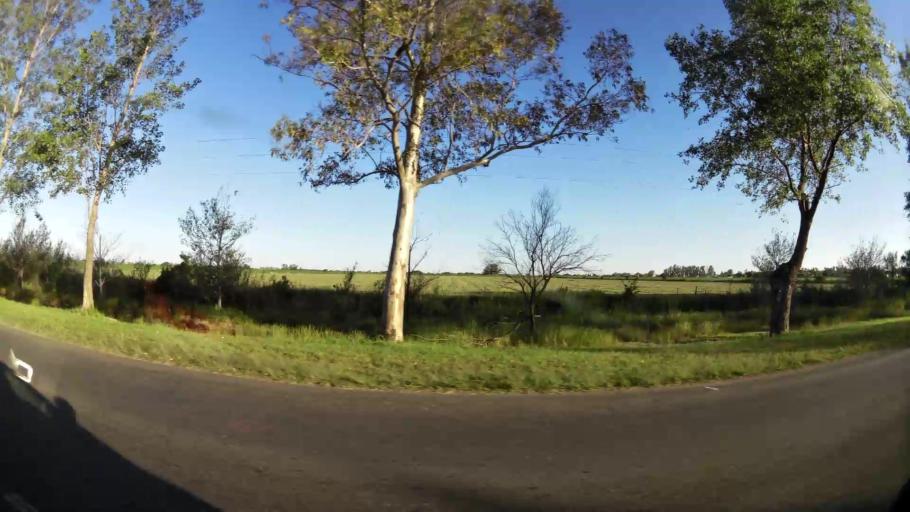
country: AR
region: Cordoba
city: Las Varillas
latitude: -31.8634
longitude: -62.7050
